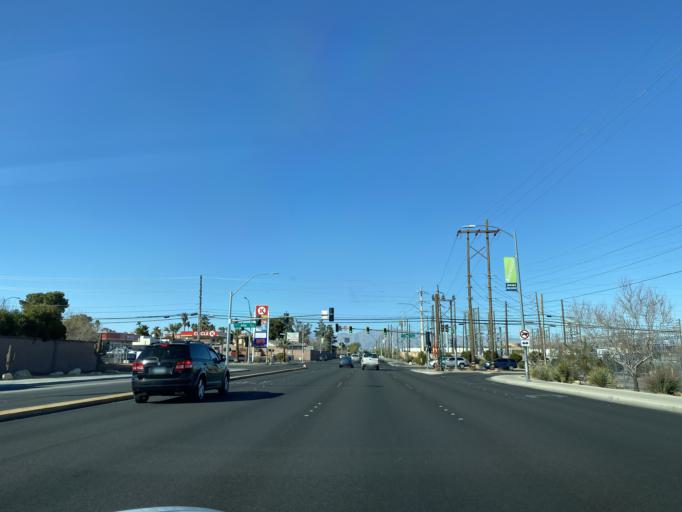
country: US
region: Nevada
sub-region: Clark County
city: Las Vegas
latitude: 36.1654
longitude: -115.1925
